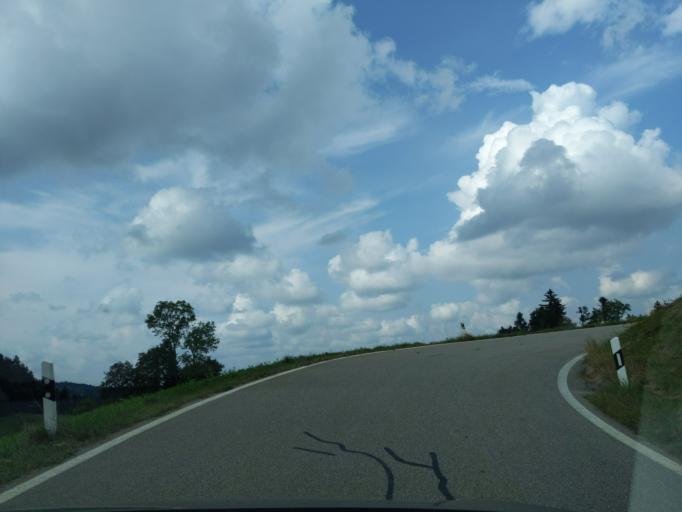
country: CH
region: Bern
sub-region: Oberaargau
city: Wyssachen
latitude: 47.0601
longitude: 7.8366
